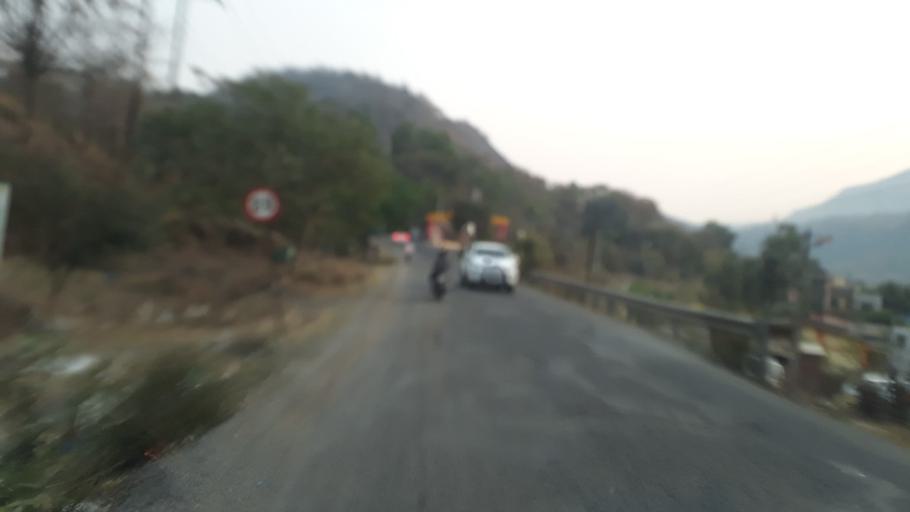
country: IN
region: Maharashtra
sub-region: Raigarh
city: Neral
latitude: 19.0194
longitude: 73.3117
